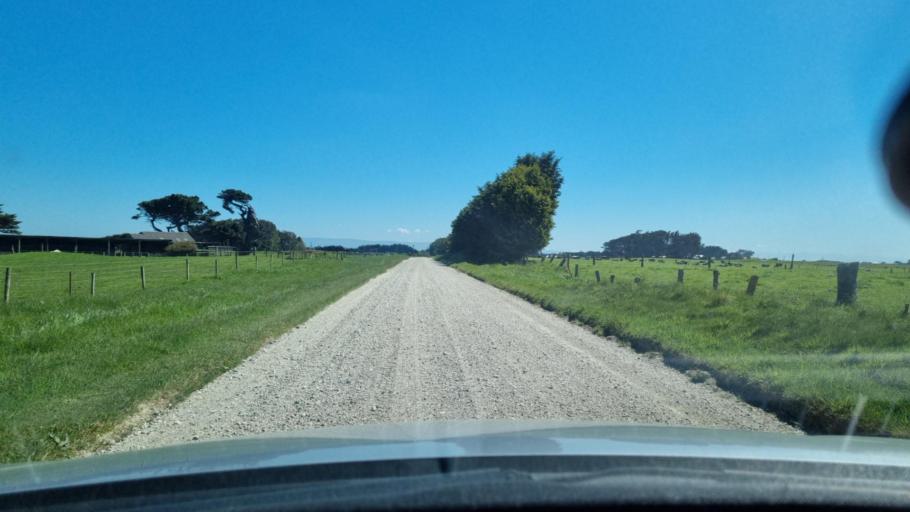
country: NZ
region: Southland
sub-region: Invercargill City
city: Invercargill
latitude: -46.4180
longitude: 168.2685
